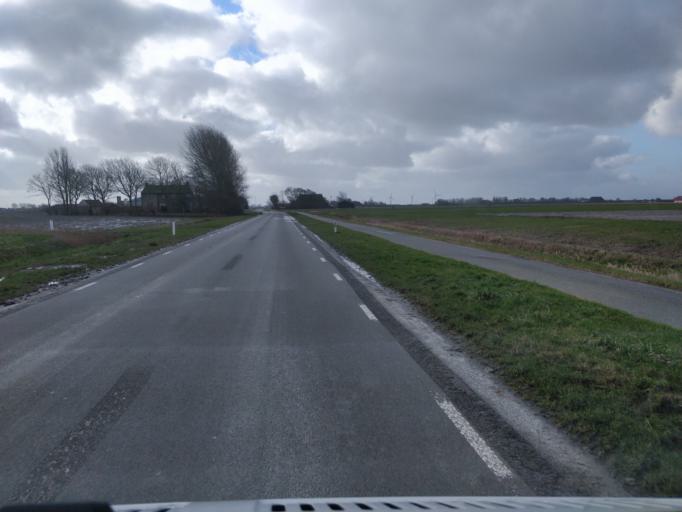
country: NL
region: Friesland
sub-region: Gemeente Franekeradeel
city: Sexbierum
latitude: 53.2106
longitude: 5.4663
